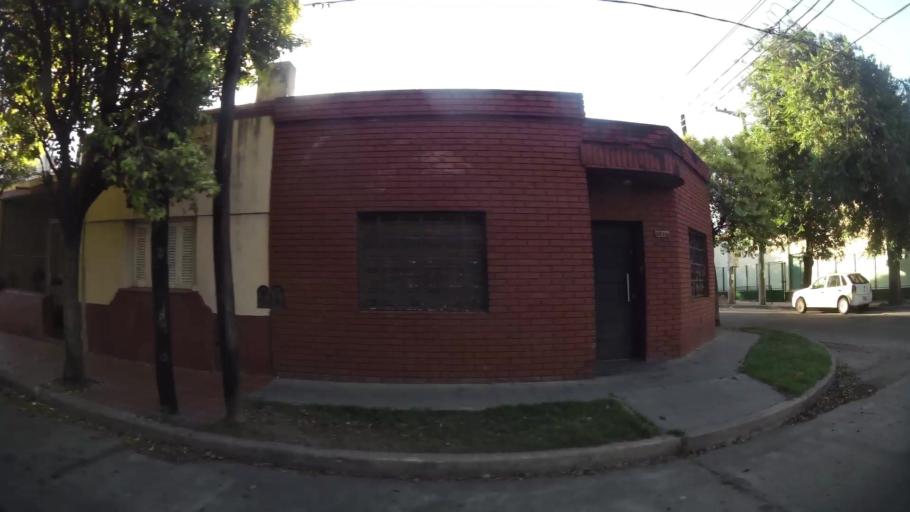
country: AR
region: Cordoba
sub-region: Departamento de Capital
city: Cordoba
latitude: -31.3751
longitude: -64.2080
